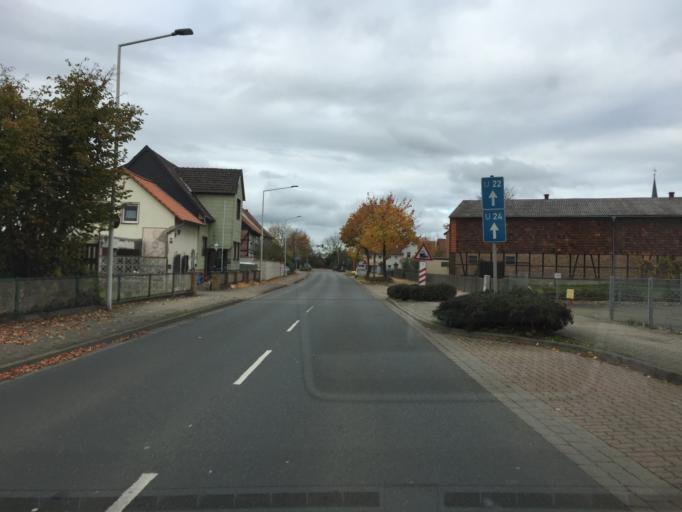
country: DE
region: Lower Saxony
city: Wolfenbuettel
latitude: 52.1726
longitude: 10.5161
